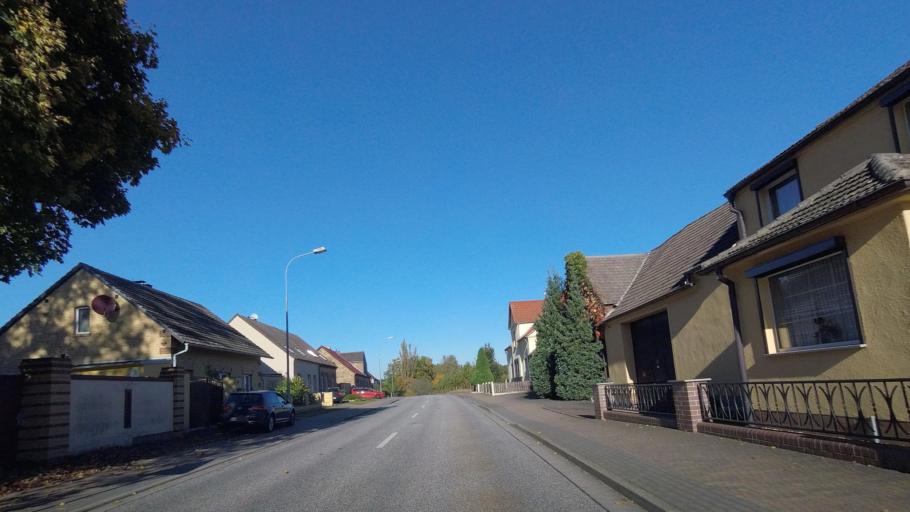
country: DE
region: Saxony-Anhalt
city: Abtsdorf
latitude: 51.8979
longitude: 12.7541
